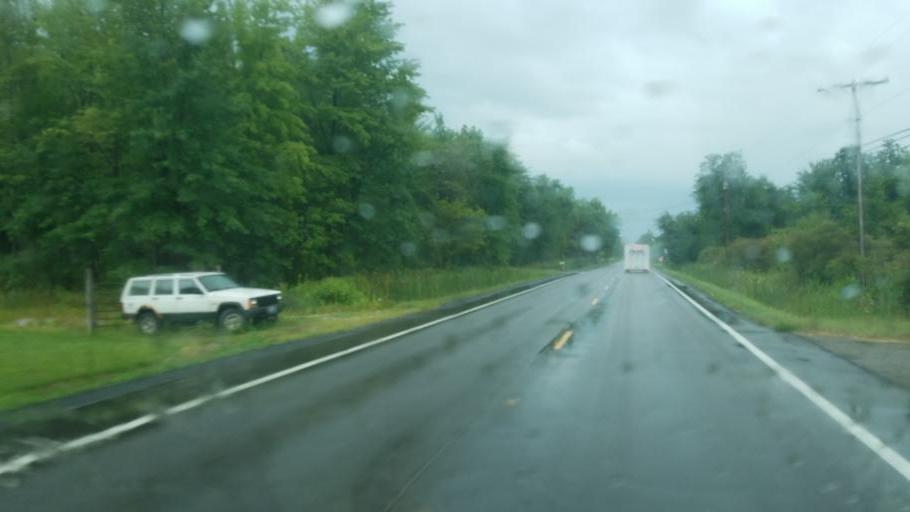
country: US
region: Ohio
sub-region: Trumbull County
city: Champion Heights
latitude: 41.3425
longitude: -80.8580
